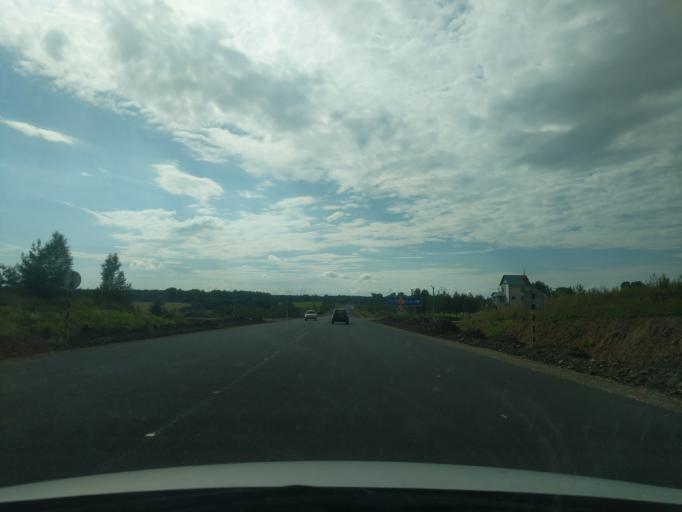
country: RU
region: Kostroma
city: Sudislavl'
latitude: 57.8106
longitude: 41.4667
